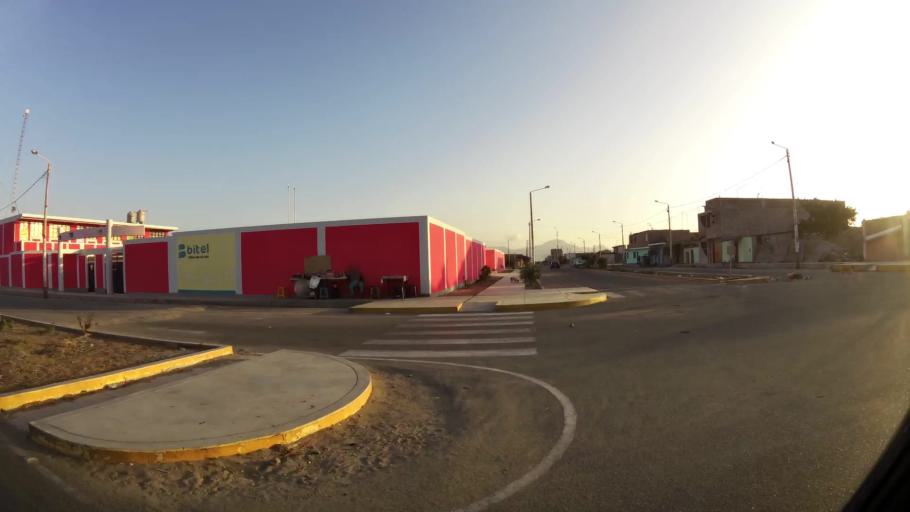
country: PE
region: Ancash
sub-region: Provincia de Santa
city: Buenos Aires
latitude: -9.1470
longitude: -78.5034
